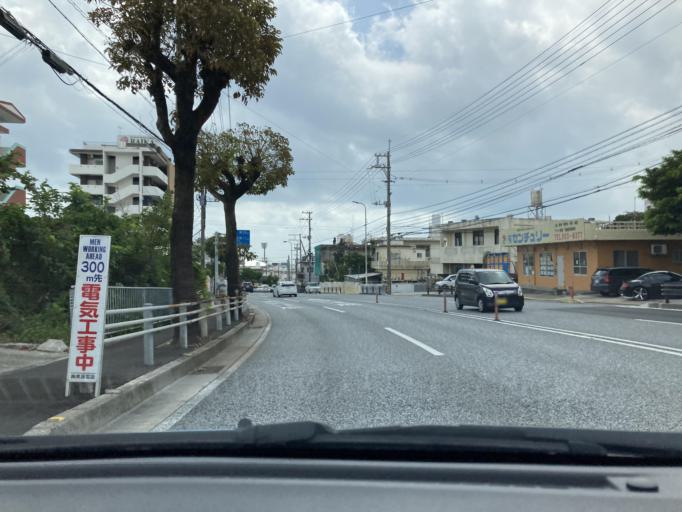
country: JP
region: Okinawa
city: Okinawa
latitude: 26.3163
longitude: 127.8188
